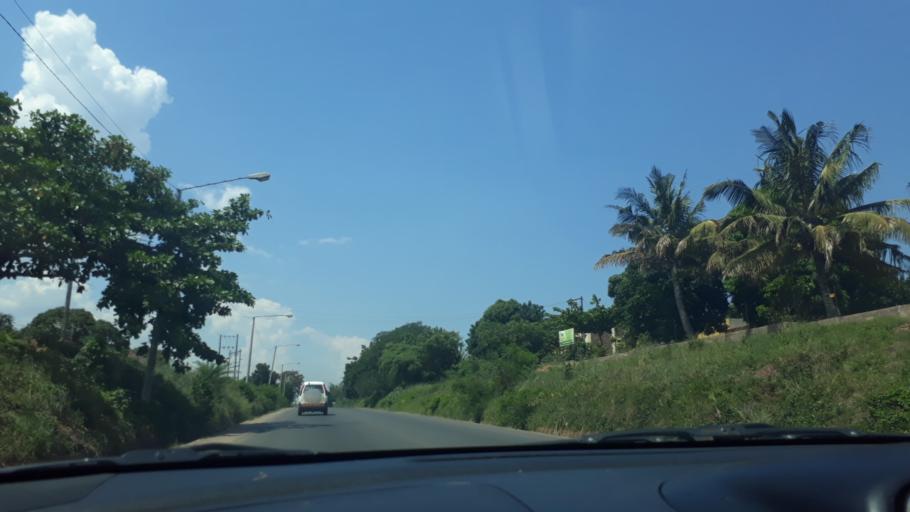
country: MZ
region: Maputo
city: Matola
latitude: -25.9619
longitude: 32.4486
